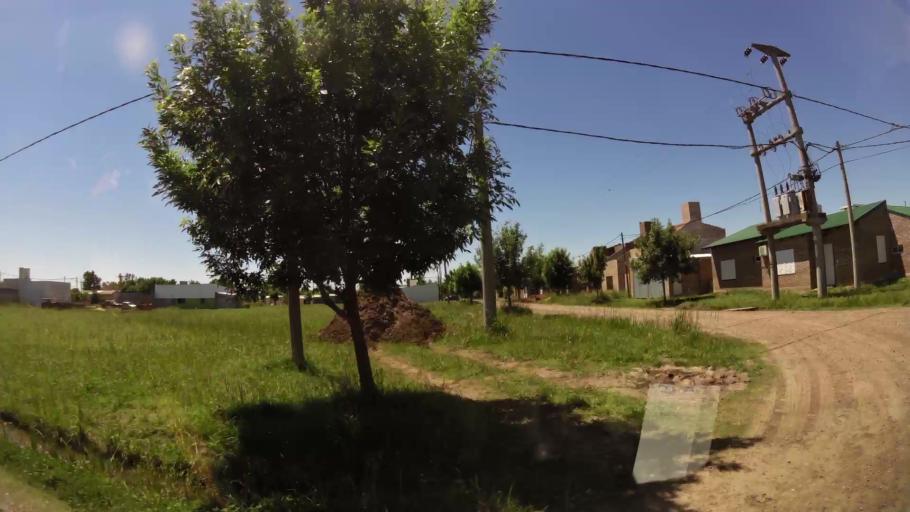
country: AR
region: Santa Fe
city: Esperanza
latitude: -31.3916
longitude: -61.0854
